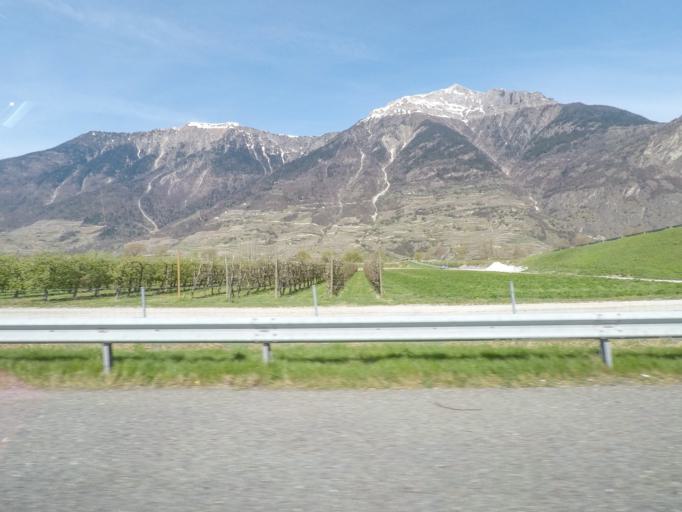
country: CH
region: Valais
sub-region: Martigny District
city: Charrat-les-Chenes
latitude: 46.1400
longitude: 7.1402
